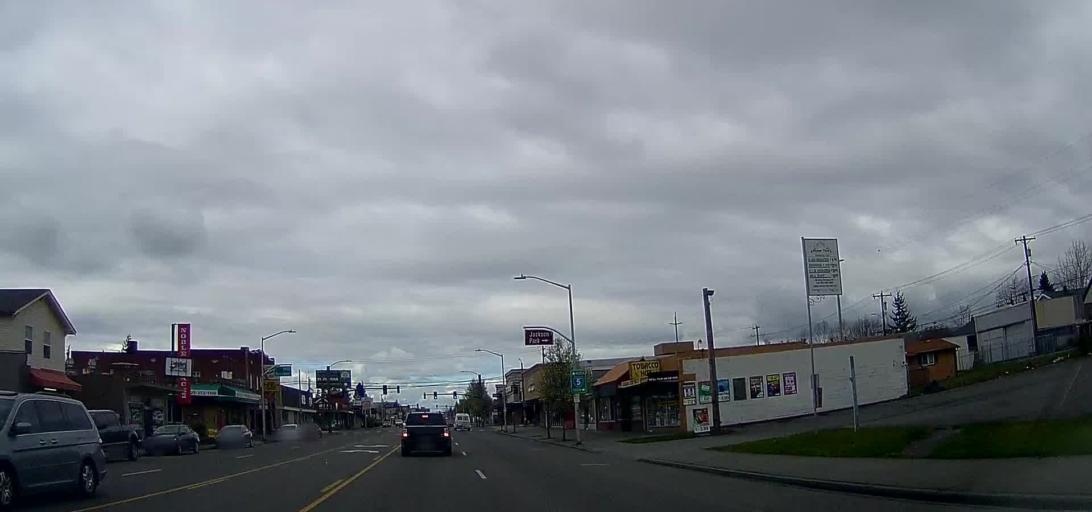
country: US
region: Washington
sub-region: Snohomish County
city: Everett
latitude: 47.9914
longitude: -122.2012
